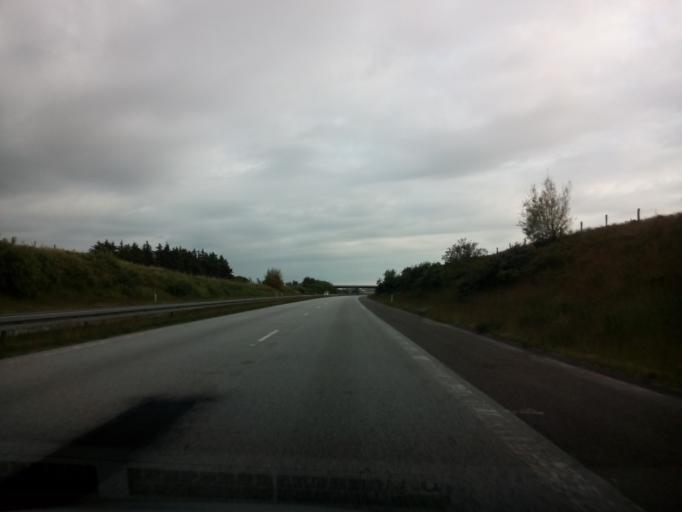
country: DK
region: North Denmark
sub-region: Hjorring Kommune
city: Hjorring
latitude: 57.3983
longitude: 10.0287
